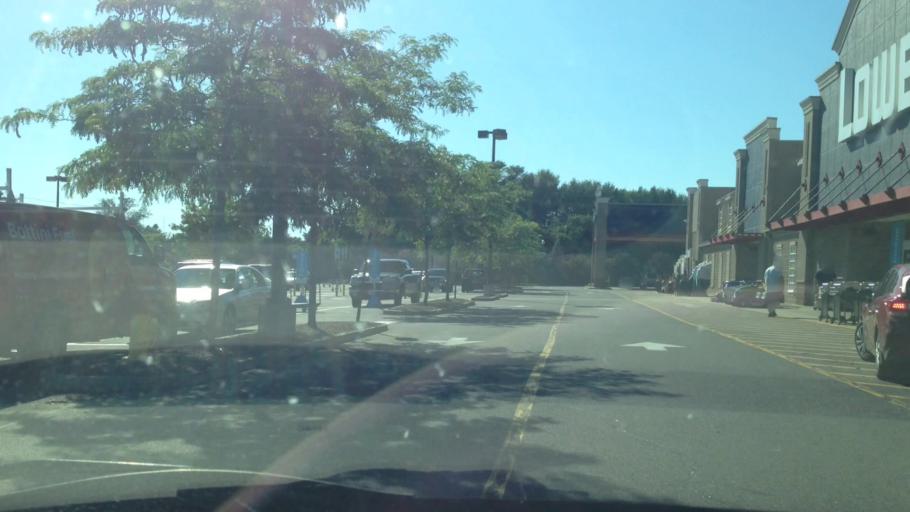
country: US
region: New York
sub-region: Ulster County
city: Clintondale
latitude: 41.7389
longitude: -74.0342
